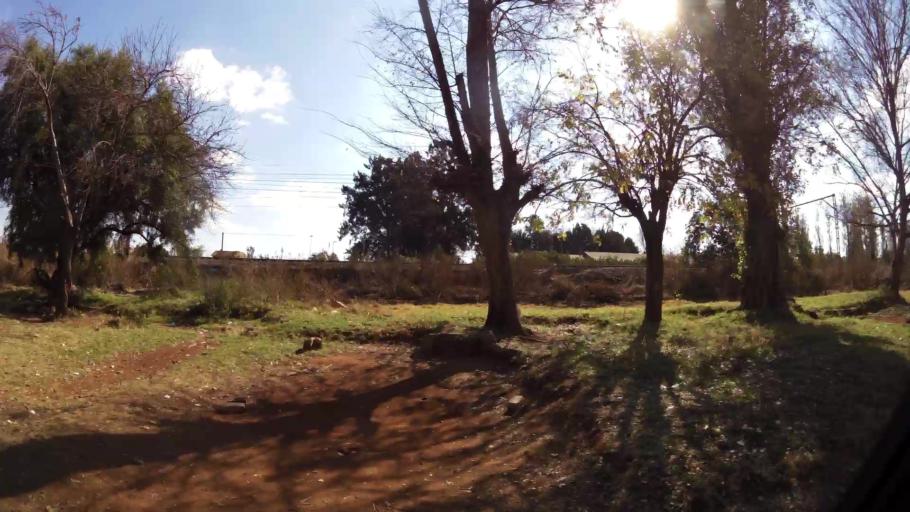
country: ZA
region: Gauteng
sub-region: City of Johannesburg Metropolitan Municipality
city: Soweto
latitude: -26.2361
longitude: 27.8735
